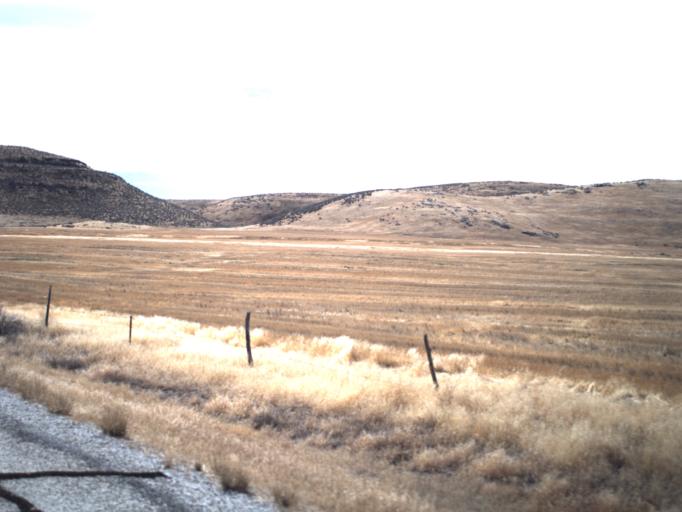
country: US
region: Utah
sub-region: Box Elder County
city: Tremonton
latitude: 41.7141
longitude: -112.4526
